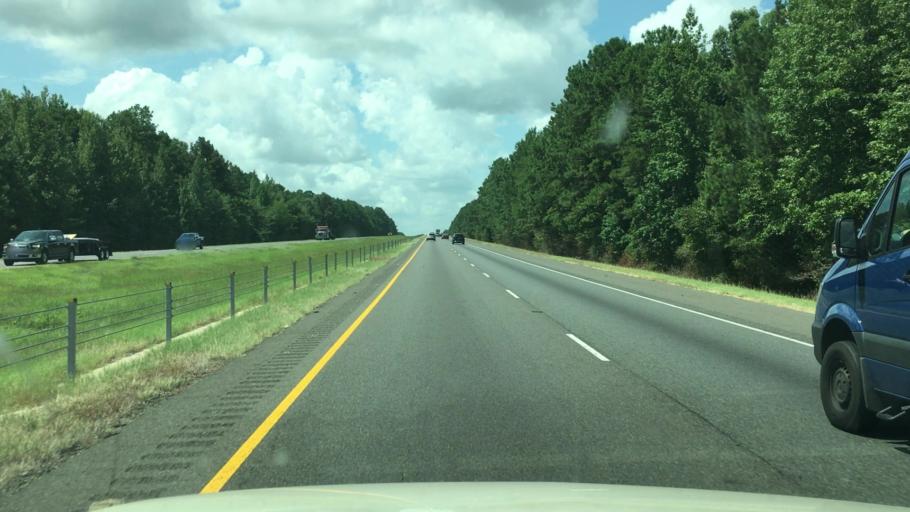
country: US
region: Arkansas
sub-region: Clark County
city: Arkadelphia
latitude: 34.0501
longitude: -93.1347
